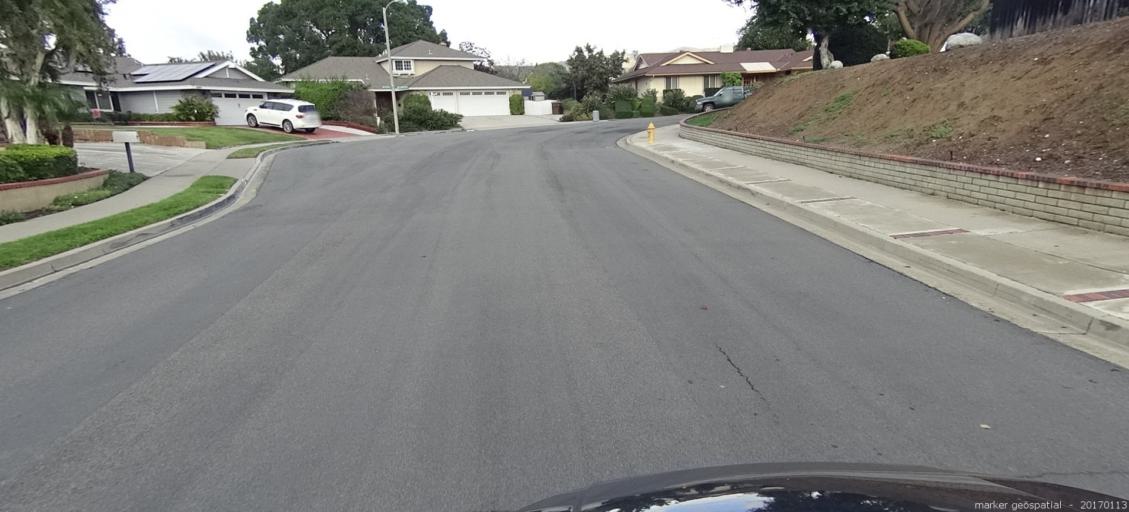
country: US
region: California
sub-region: Orange County
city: Yorba Linda
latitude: 33.8877
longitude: -117.7968
